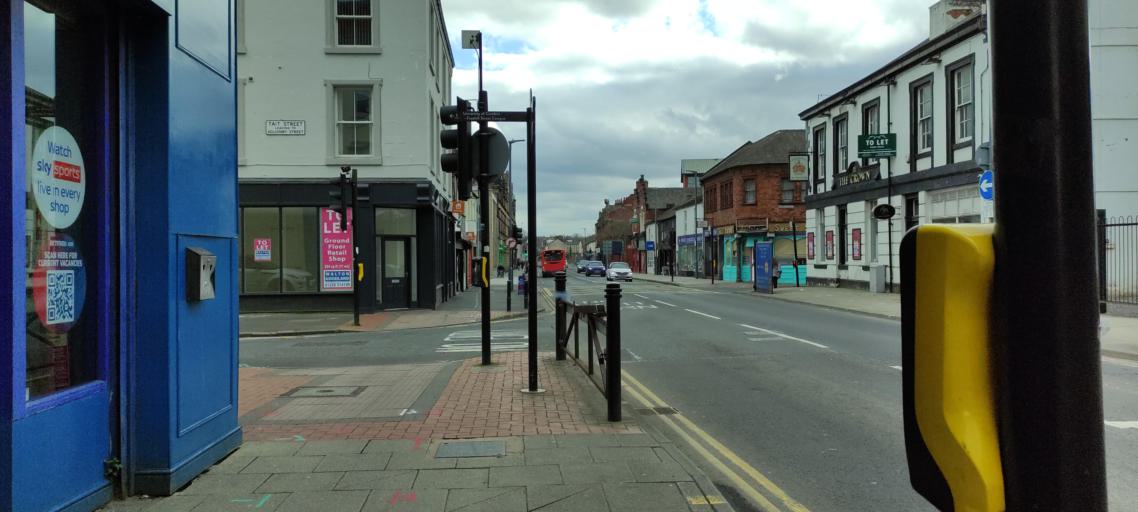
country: GB
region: England
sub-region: Cumbria
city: Carlisle
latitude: 54.8905
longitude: -2.9298
